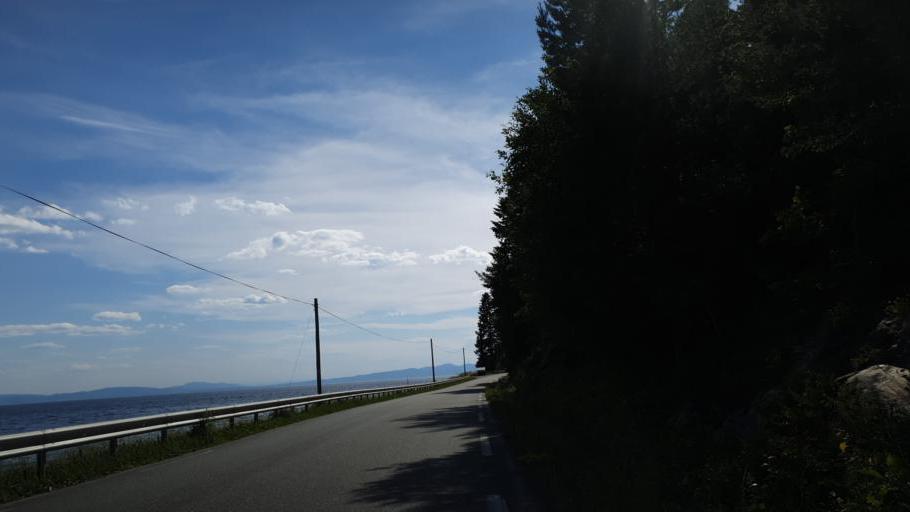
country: NO
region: Nord-Trondelag
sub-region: Leksvik
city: Leksvik
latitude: 63.6411
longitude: 10.5898
